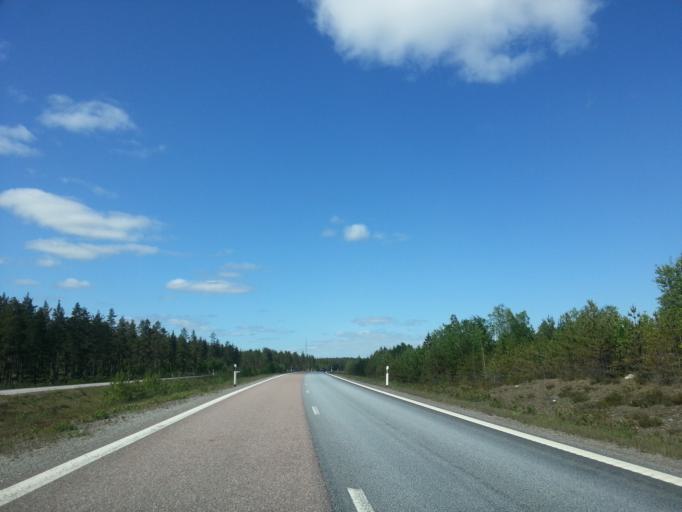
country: SE
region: Gaevleborg
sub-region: Soderhamns Kommun
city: Soderhamn
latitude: 61.4569
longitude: 16.9896
